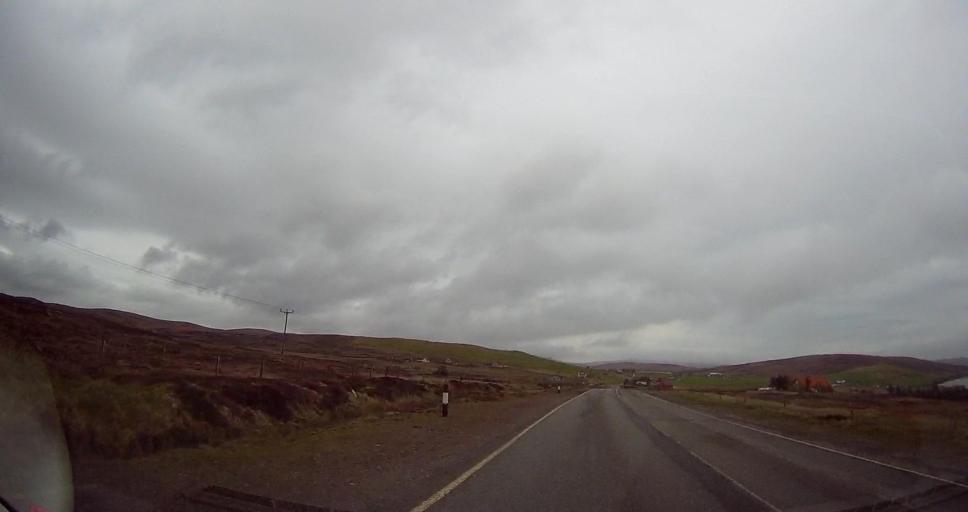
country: GB
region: Scotland
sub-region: Shetland Islands
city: Lerwick
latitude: 60.2306
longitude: -1.2372
